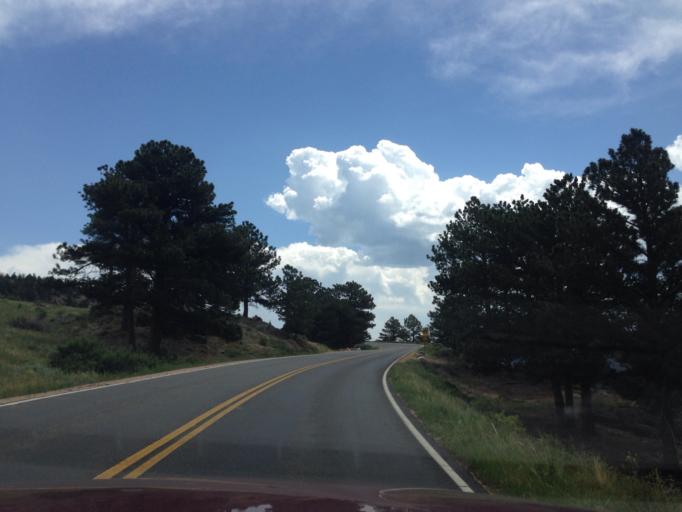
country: US
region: Colorado
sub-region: Larimer County
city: Estes Park
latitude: 40.3704
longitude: -105.5884
